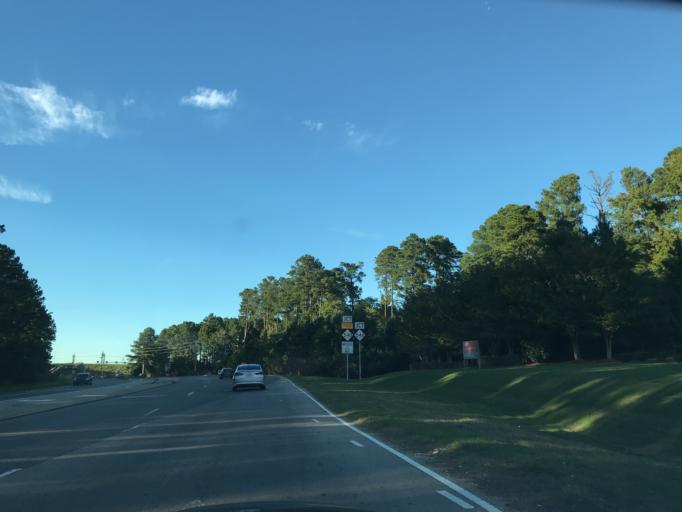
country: US
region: North Carolina
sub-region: Wake County
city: Morrisville
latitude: 35.8568
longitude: -78.8426
